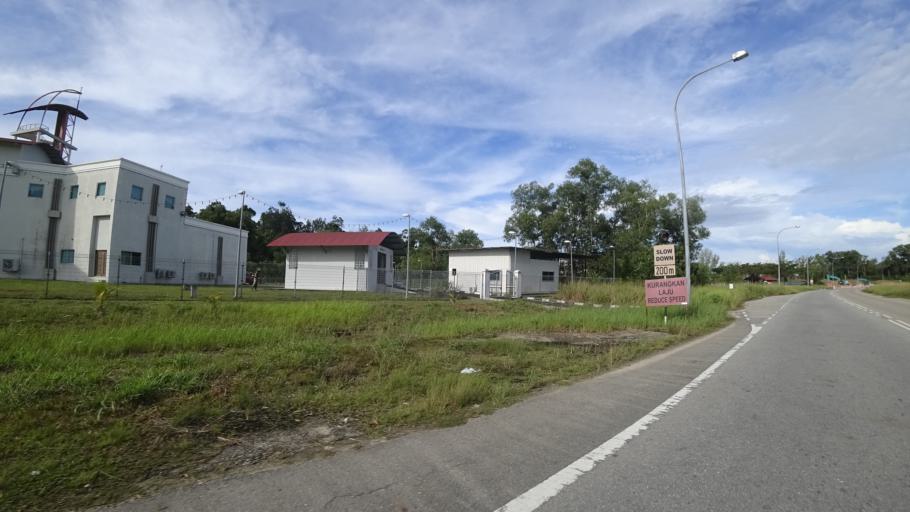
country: BN
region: Brunei and Muara
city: Bandar Seri Begawan
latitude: 4.9532
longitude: 114.9092
